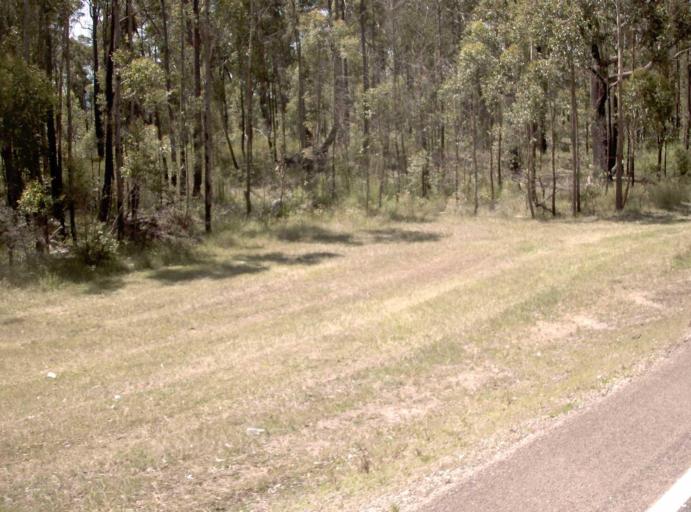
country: AU
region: New South Wales
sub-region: Bombala
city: Bombala
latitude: -37.5662
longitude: 149.1146
